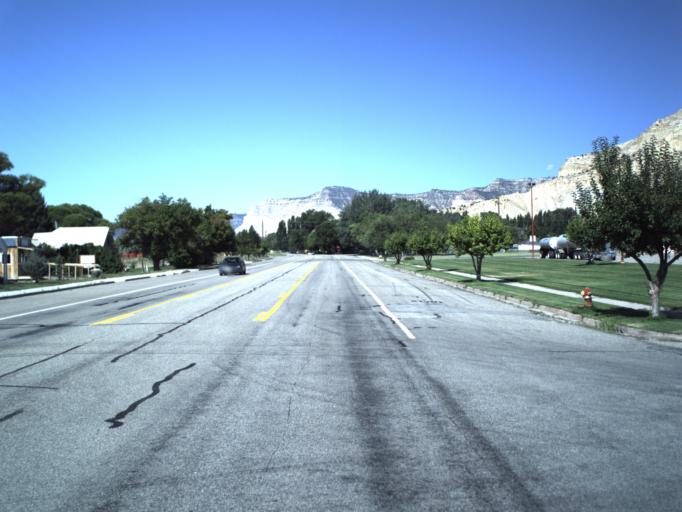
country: US
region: Utah
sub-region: Emery County
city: Ferron
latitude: 38.9232
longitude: -111.2486
